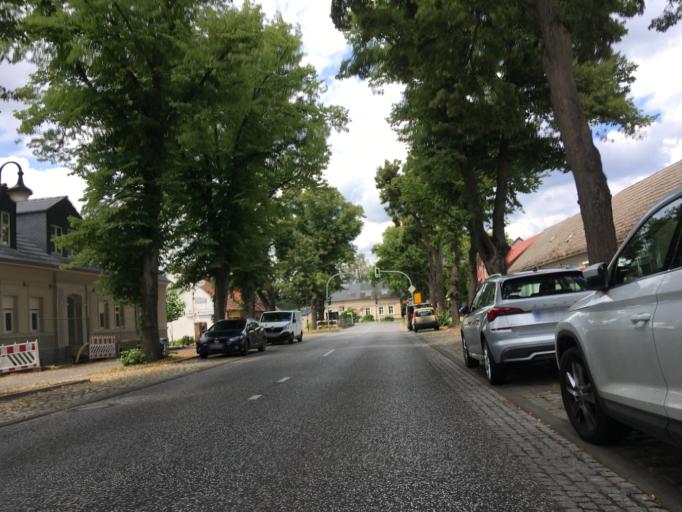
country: DE
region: Berlin
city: Buch
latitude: 52.6557
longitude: 13.5395
